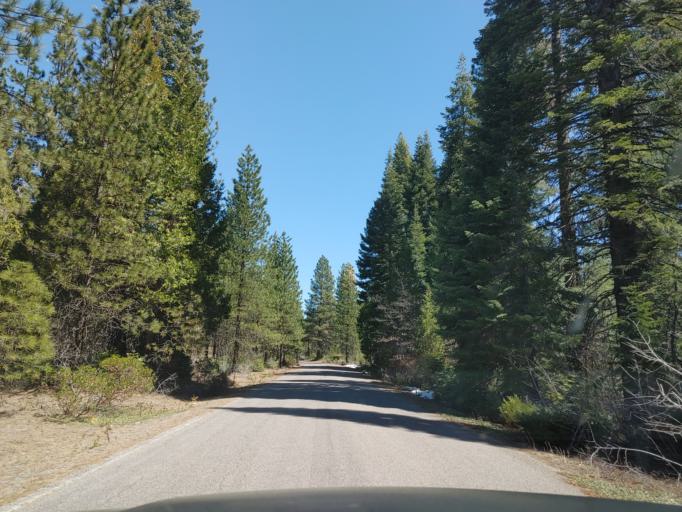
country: US
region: California
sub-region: Siskiyou County
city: McCloud
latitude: 41.2505
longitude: -121.9510
